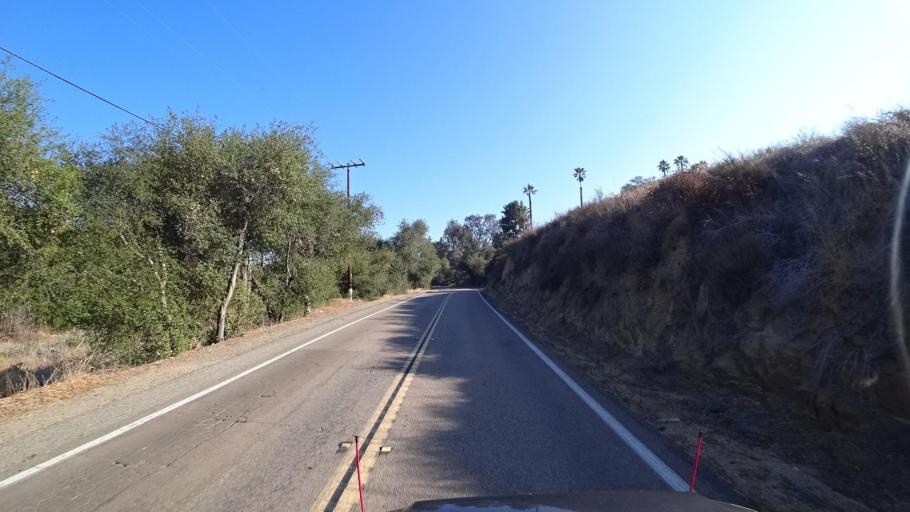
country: US
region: California
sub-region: San Diego County
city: Bonsall
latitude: 33.2991
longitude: -117.2423
